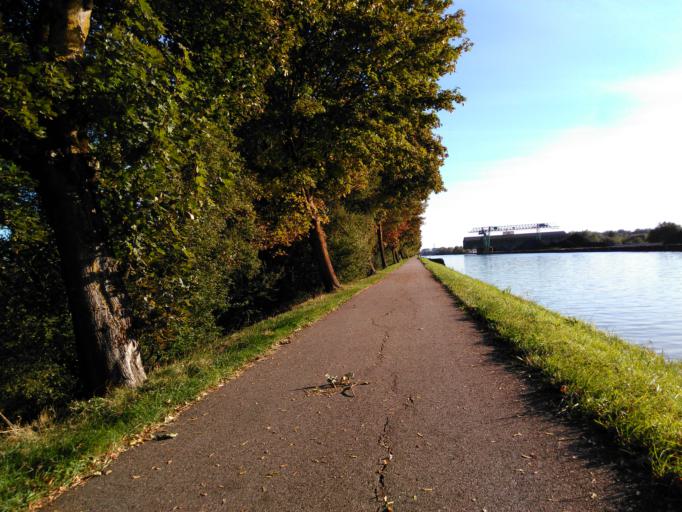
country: FR
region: Lorraine
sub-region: Departement de la Moselle
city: Bousse
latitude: 49.2748
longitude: 6.1820
